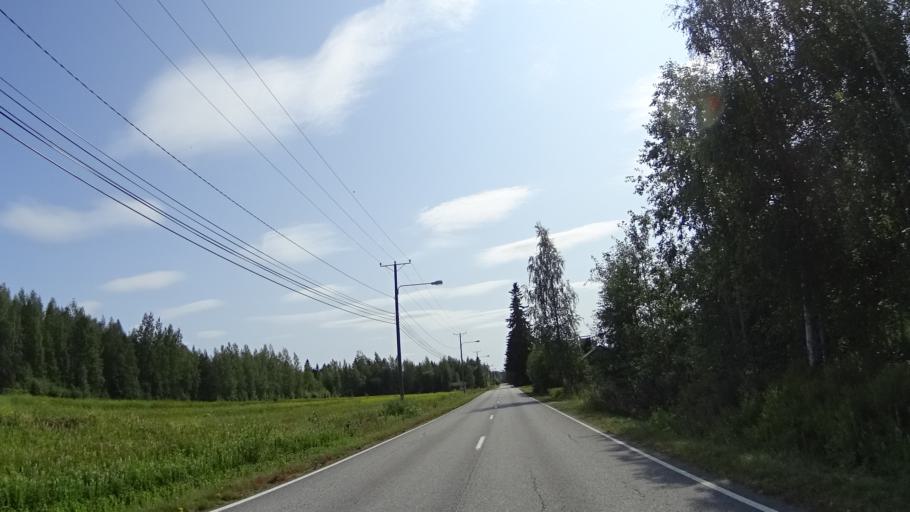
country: FI
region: Pirkanmaa
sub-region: Ylae-Pirkanmaa
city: Maenttae
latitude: 61.9160
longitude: 24.7743
